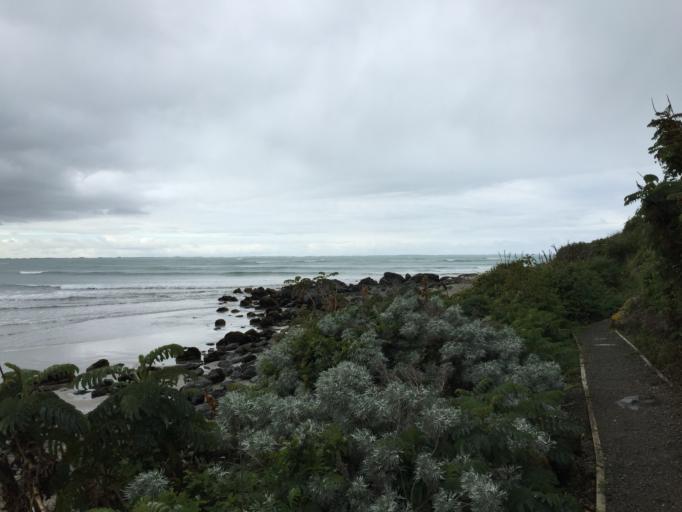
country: NZ
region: Southland
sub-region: Southland District
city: Riverton
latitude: -46.3721
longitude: 168.0285
